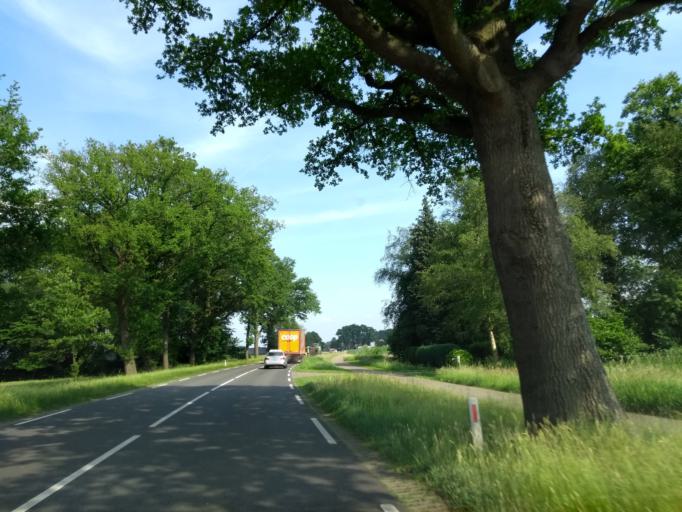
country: DE
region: Lower Saxony
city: Lage
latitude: 52.4083
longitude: 6.9164
